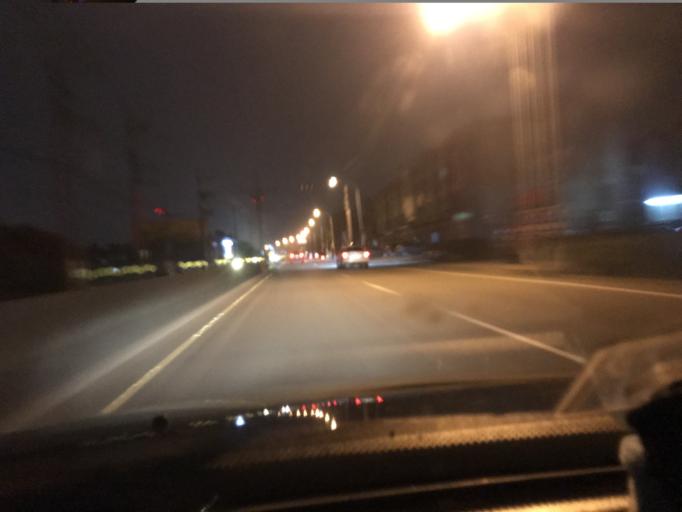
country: TW
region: Taiwan
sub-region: Hsinchu
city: Zhubei
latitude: 24.7800
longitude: 121.0698
